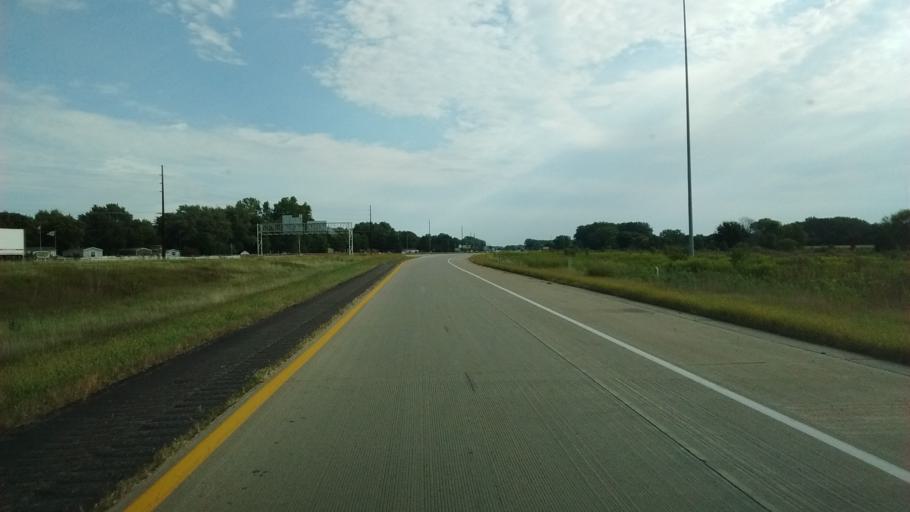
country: US
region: Iowa
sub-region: Woodbury County
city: Sioux City
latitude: 42.5562
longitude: -96.3386
